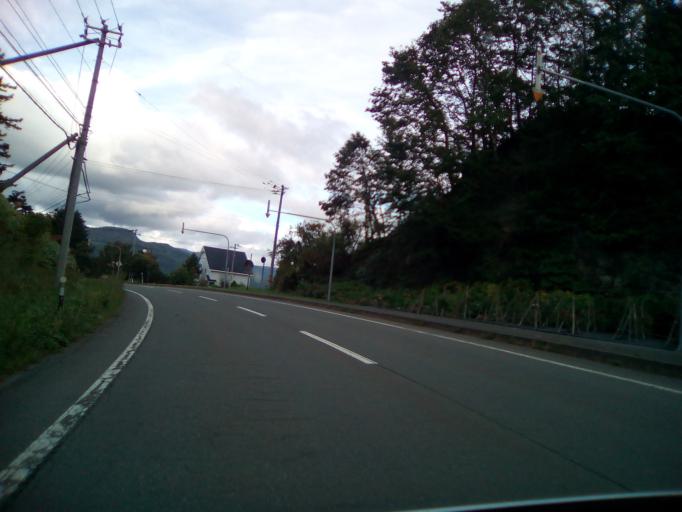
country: JP
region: Hokkaido
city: Date
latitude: 42.6434
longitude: 140.8470
